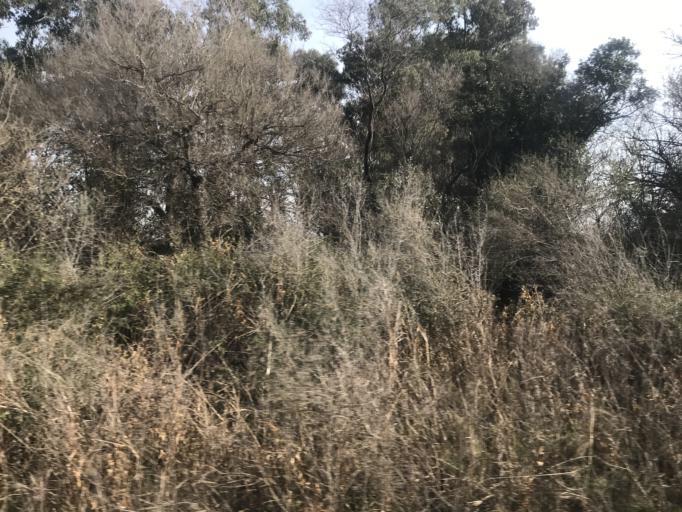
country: AR
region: Cordoba
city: Laguna Larga
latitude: -31.7663
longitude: -63.8123
